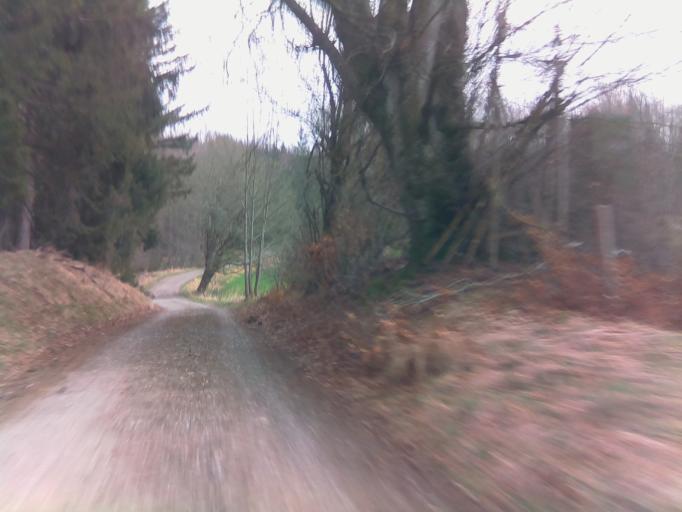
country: DE
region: Bavaria
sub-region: Upper Bavaria
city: Ingenried
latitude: 47.8468
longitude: 10.7988
